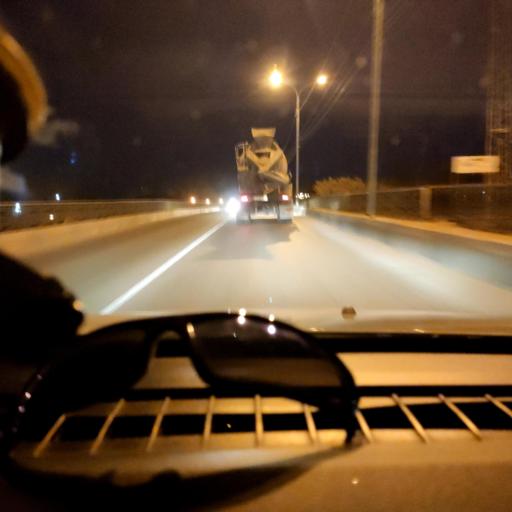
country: RU
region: Samara
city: Novokuybyshevsk
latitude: 53.1157
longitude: 50.0621
